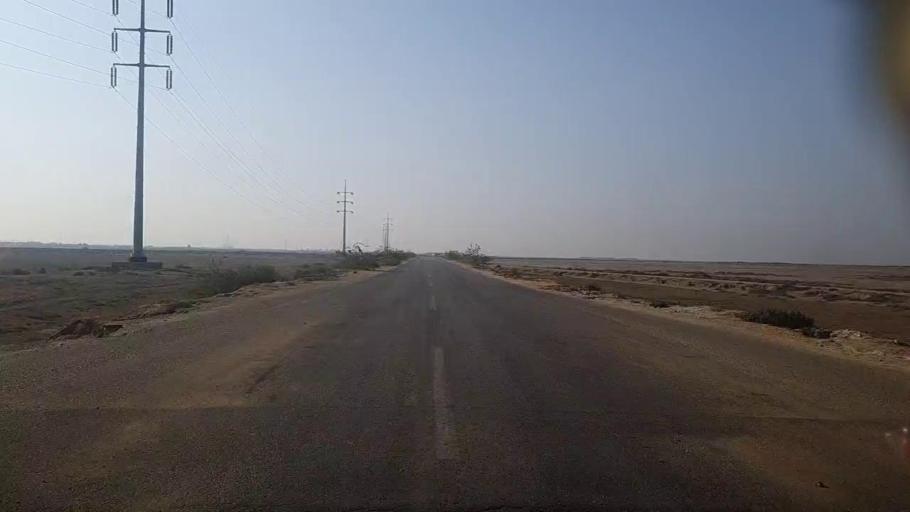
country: PK
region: Sindh
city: Gharo
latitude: 24.7382
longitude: 67.5350
